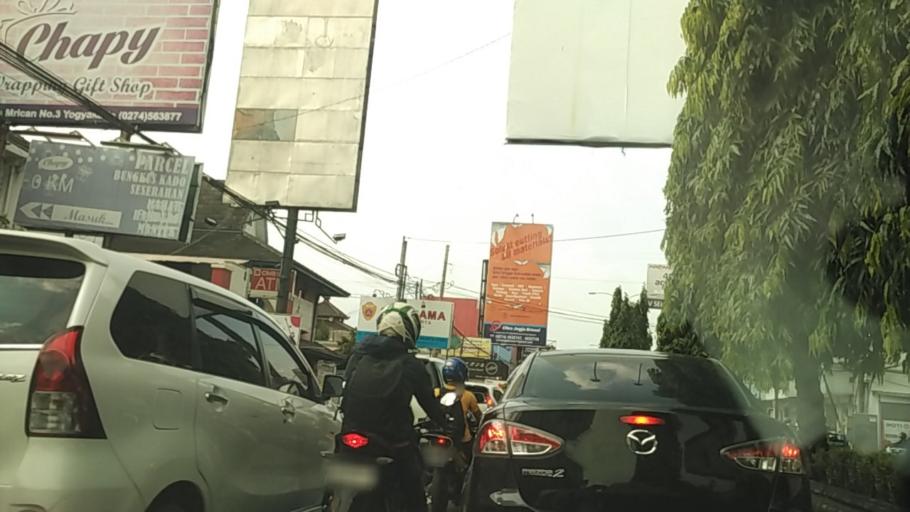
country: ID
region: Daerah Istimewa Yogyakarta
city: Yogyakarta
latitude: -7.7744
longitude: 110.3893
